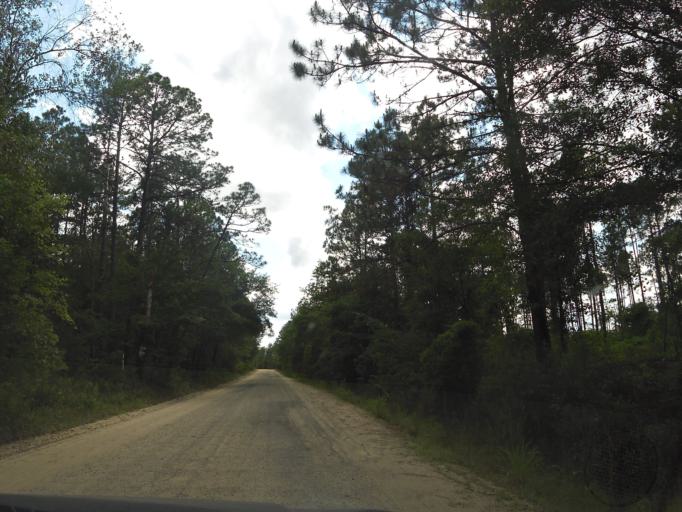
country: US
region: Florida
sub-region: Clay County
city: Asbury Lake
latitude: 29.8958
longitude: -81.8612
